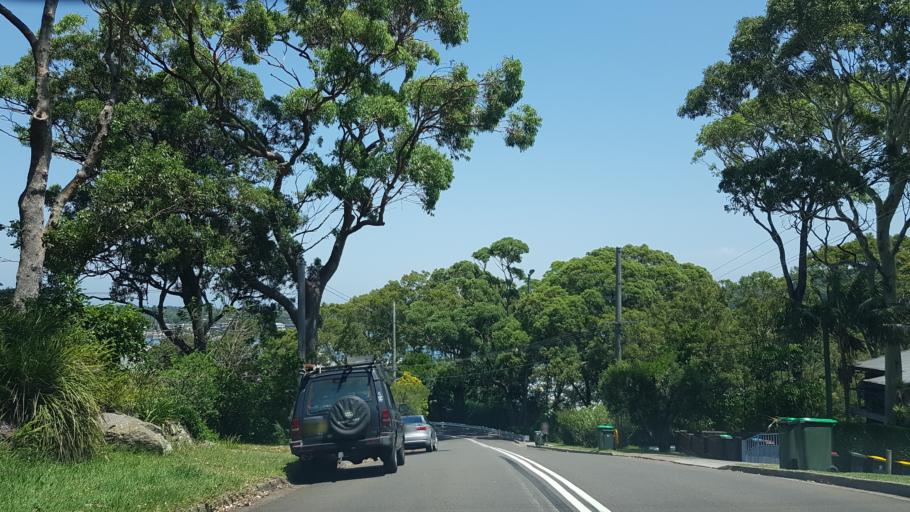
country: AU
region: New South Wales
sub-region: Pittwater
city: Bay View
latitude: -33.6534
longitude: 151.3051
